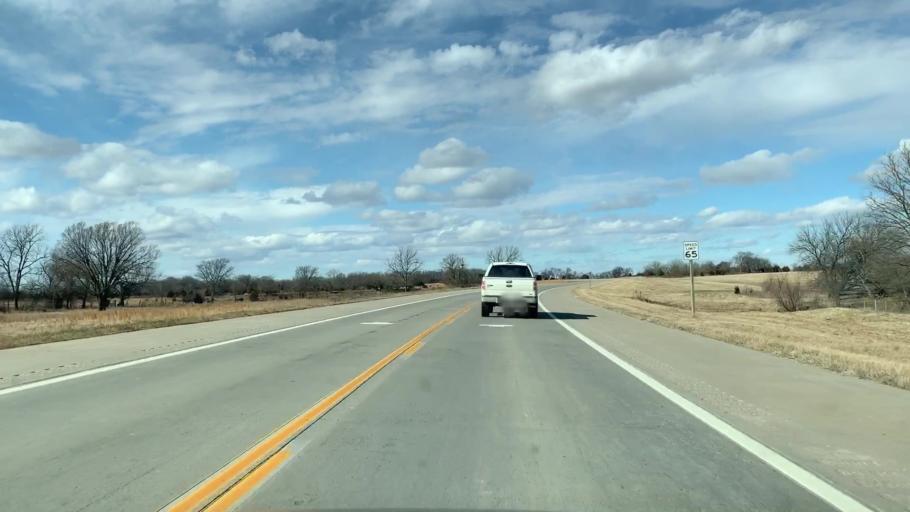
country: US
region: Kansas
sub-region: Labette County
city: Parsons
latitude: 37.3436
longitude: -95.1832
